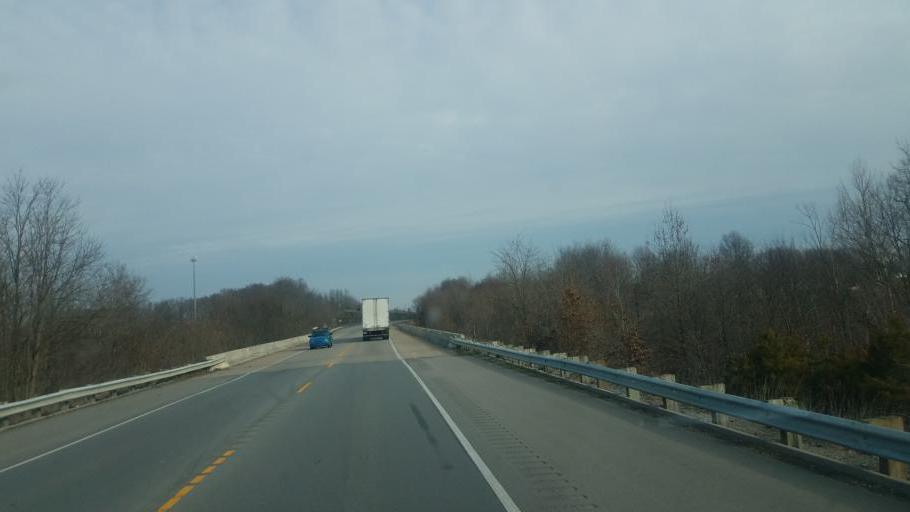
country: US
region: Kentucky
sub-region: Boyle County
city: Junction City
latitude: 37.5674
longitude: -84.7964
